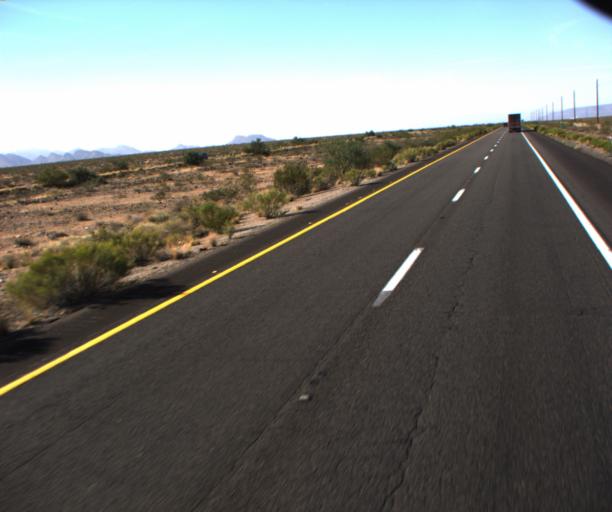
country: US
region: Arizona
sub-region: Mohave County
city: Kingman
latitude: 35.0629
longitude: -114.1253
